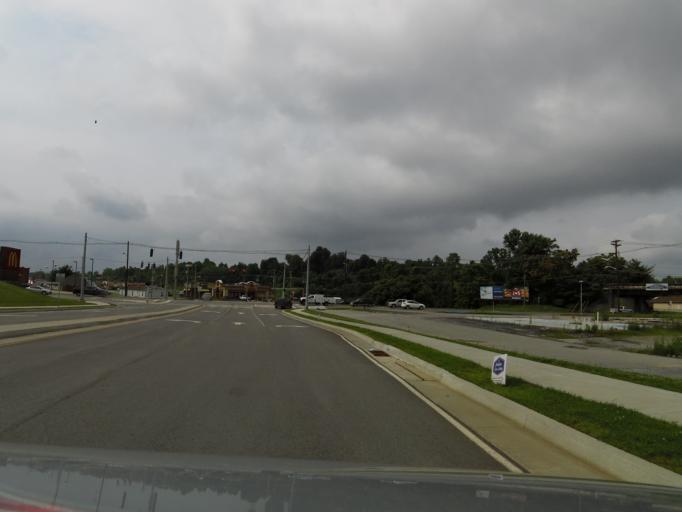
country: US
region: Kentucky
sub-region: Hopkins County
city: Madisonville
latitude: 37.3278
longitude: -87.4806
